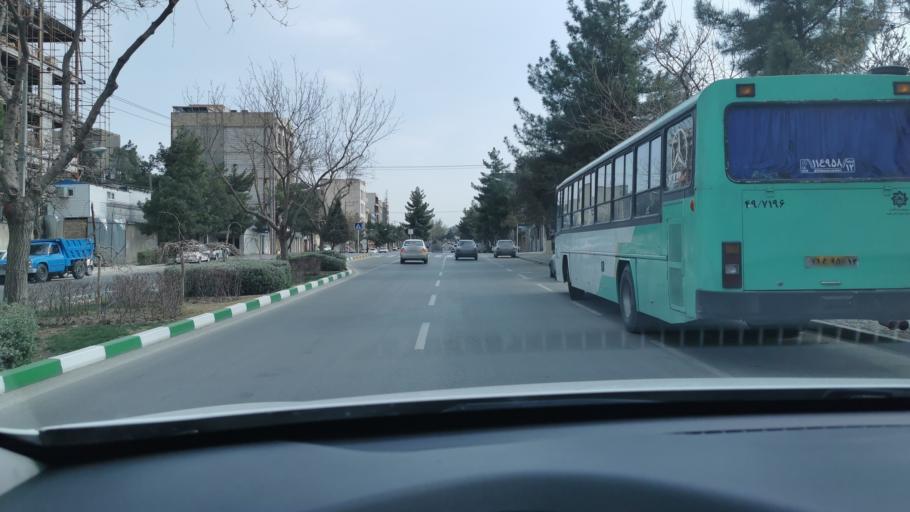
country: IR
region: Razavi Khorasan
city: Mashhad
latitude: 36.2782
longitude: 59.5653
